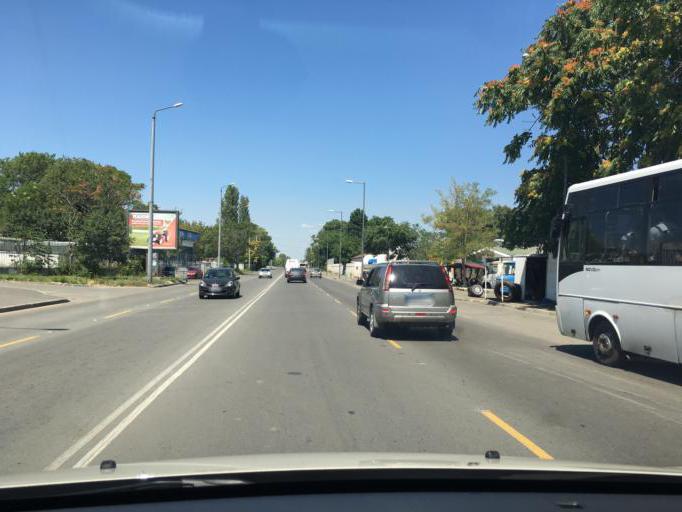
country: BG
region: Burgas
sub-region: Obshtina Burgas
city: Burgas
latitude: 42.4911
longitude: 27.4539
